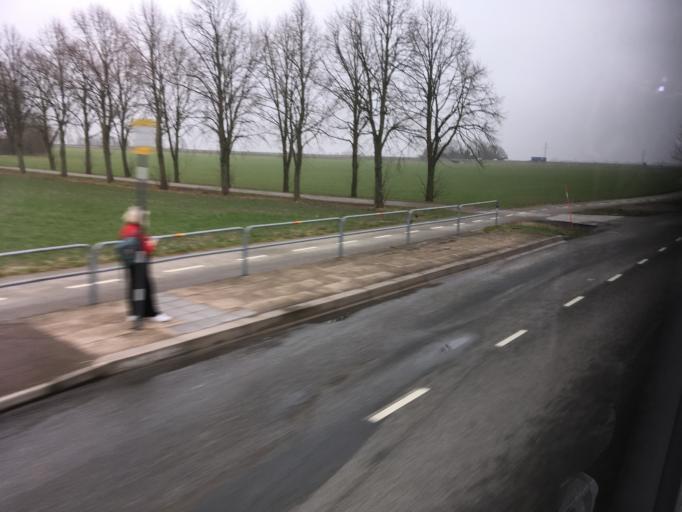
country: SE
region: Skane
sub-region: Staffanstorps Kommun
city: Hjaerup
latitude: 55.6633
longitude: 13.1459
